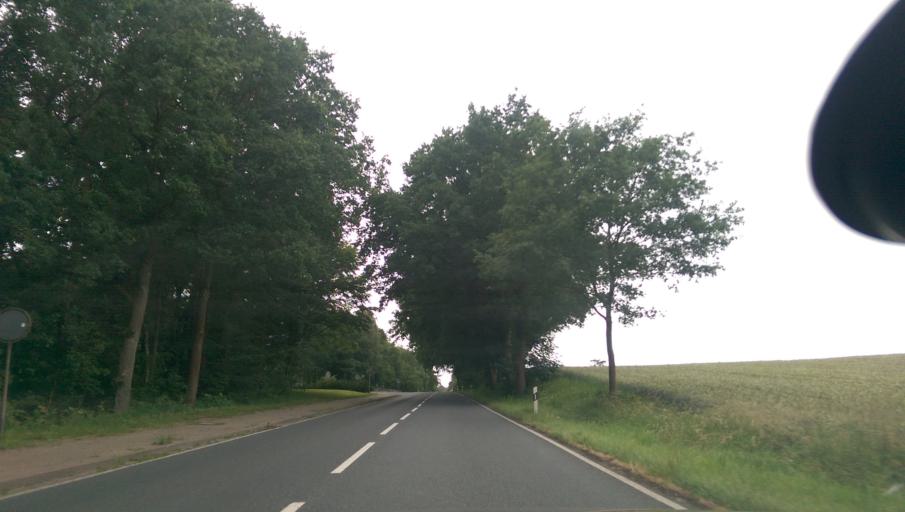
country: DE
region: Lower Saxony
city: Visselhovede
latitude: 52.9760
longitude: 9.5985
